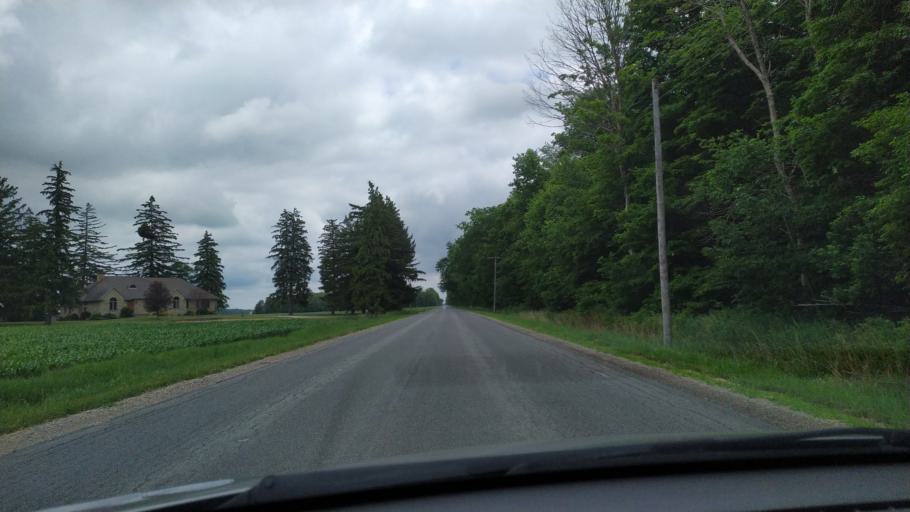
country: CA
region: Ontario
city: Stratford
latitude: 43.4070
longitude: -80.9100
